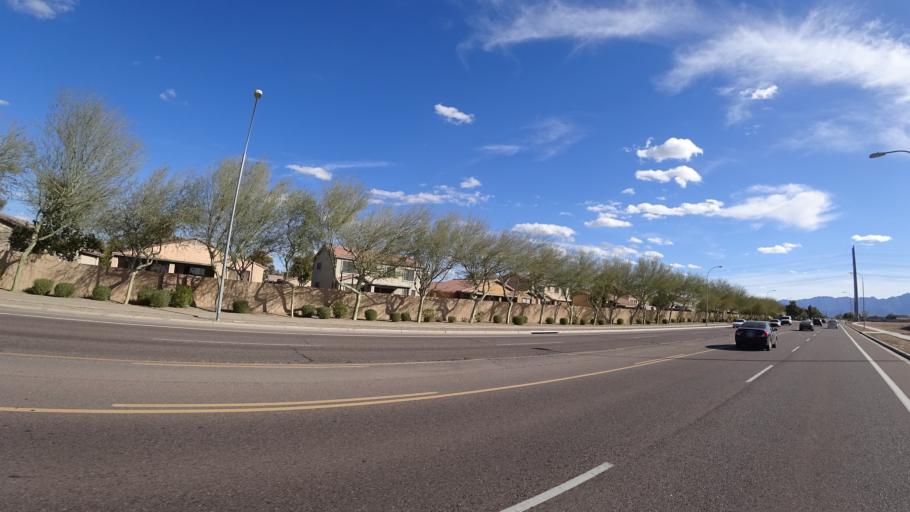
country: US
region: Arizona
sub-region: Maricopa County
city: Tolleson
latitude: 33.4180
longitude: -112.2213
